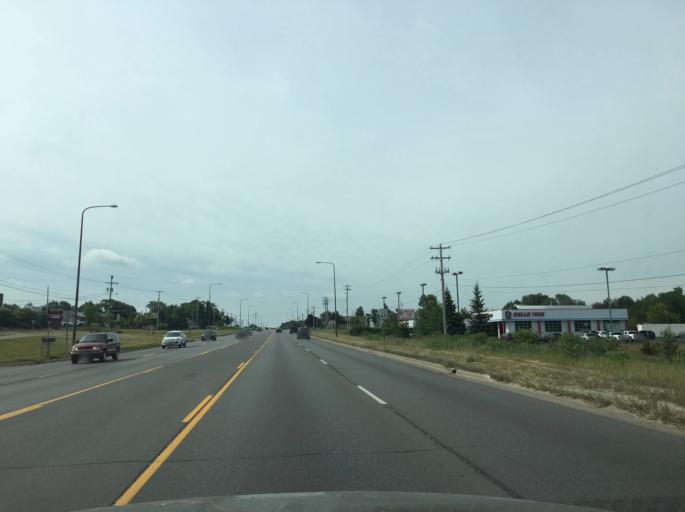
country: US
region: Michigan
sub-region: Grand Traverse County
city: Traverse City
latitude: 44.7307
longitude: -85.6462
